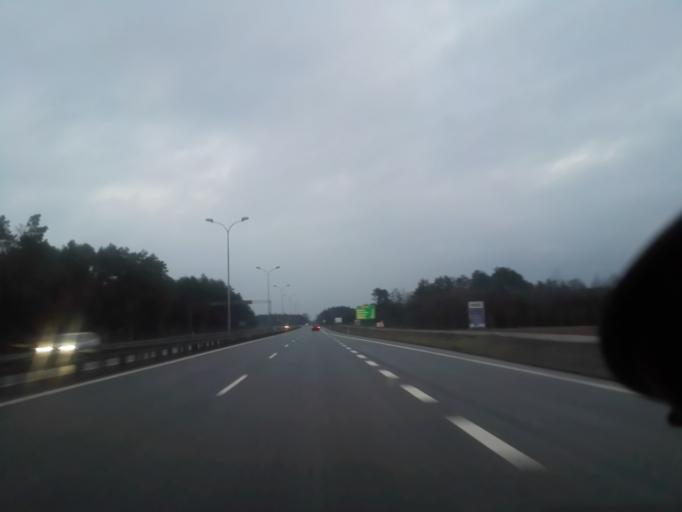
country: PL
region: Masovian Voivodeship
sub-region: Powiat wyszkowski
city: Wyszkow
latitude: 52.5358
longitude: 21.4319
